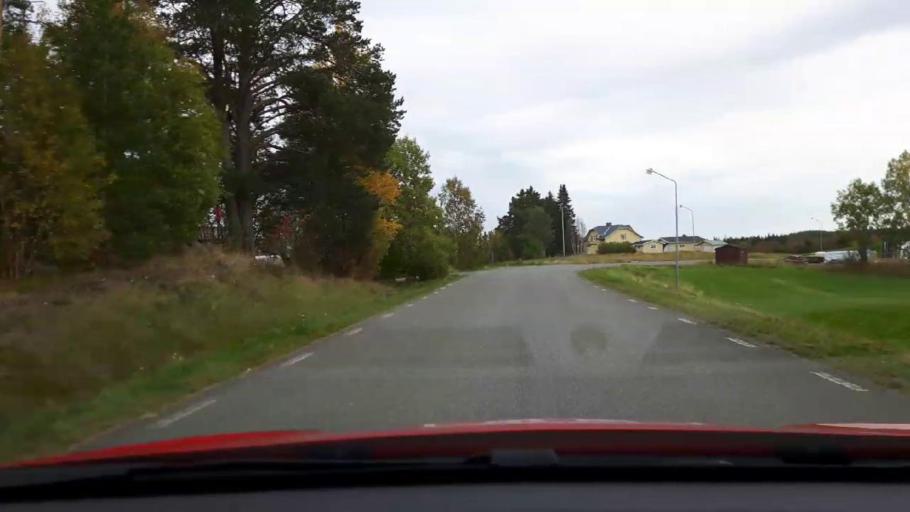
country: SE
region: Jaemtland
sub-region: Krokoms Kommun
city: Krokom
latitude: 63.2263
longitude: 14.1332
